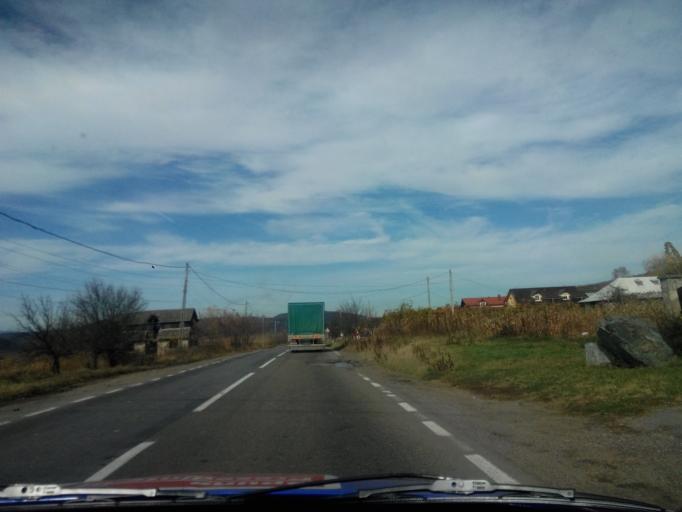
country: RO
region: Bacau
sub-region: Comuna Helegiu
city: Helegiu
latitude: 46.3669
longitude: 26.7359
